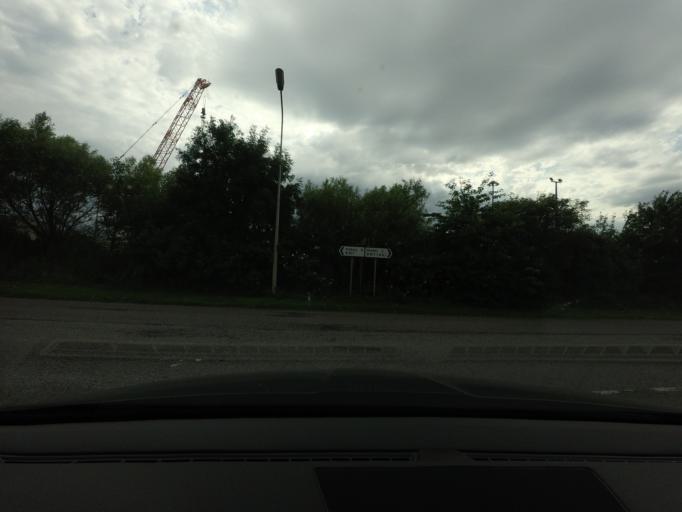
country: GB
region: Scotland
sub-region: Highland
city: Invergordon
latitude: 57.6879
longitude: -4.1767
